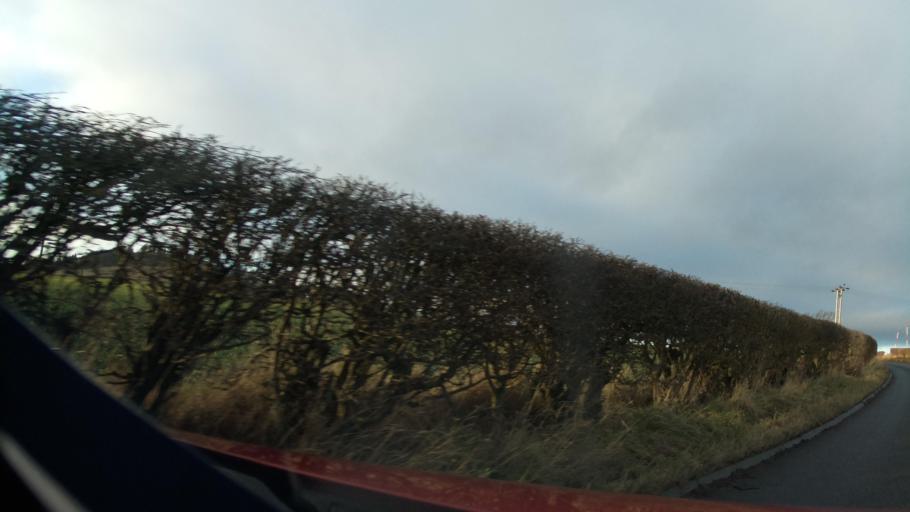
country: GB
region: Scotland
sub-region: Fife
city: Tayport
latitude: 56.5036
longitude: -2.8114
